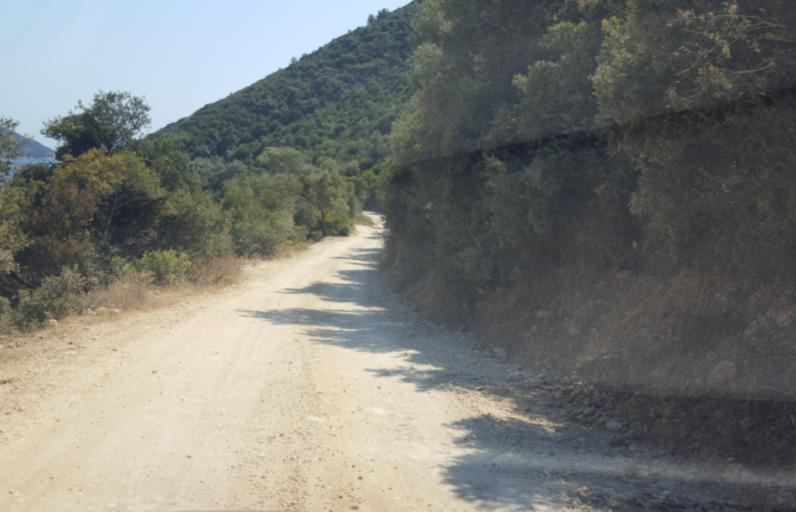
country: GR
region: Ionian Islands
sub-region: Lefkada
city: Nidri
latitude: 38.6661
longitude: 20.7123
